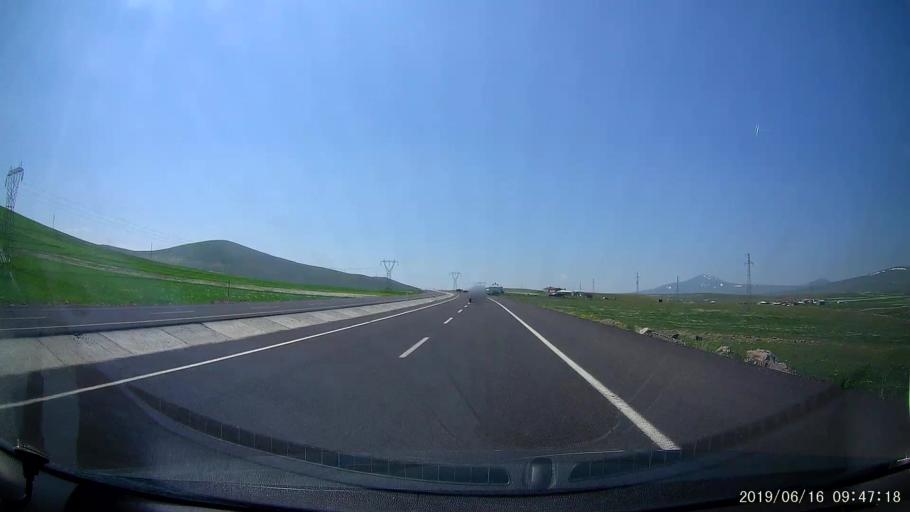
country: TR
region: Kars
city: Digor
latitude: 40.4502
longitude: 43.3426
